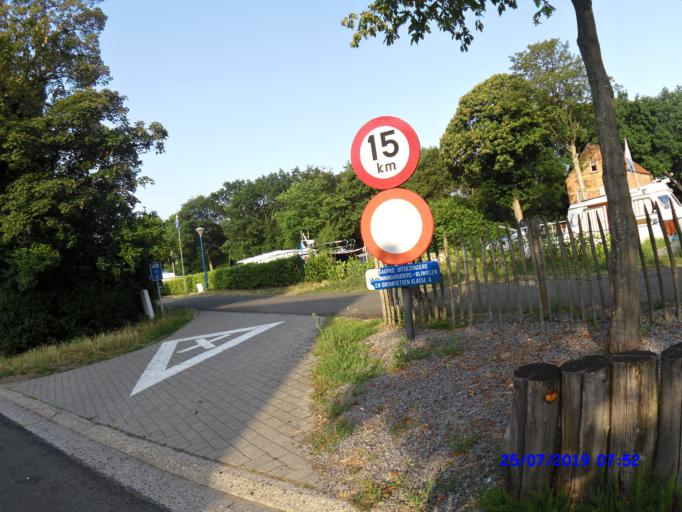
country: BE
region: Flanders
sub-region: Provincie Limburg
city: Leopoldsburg
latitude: 51.1646
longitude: 5.2609
